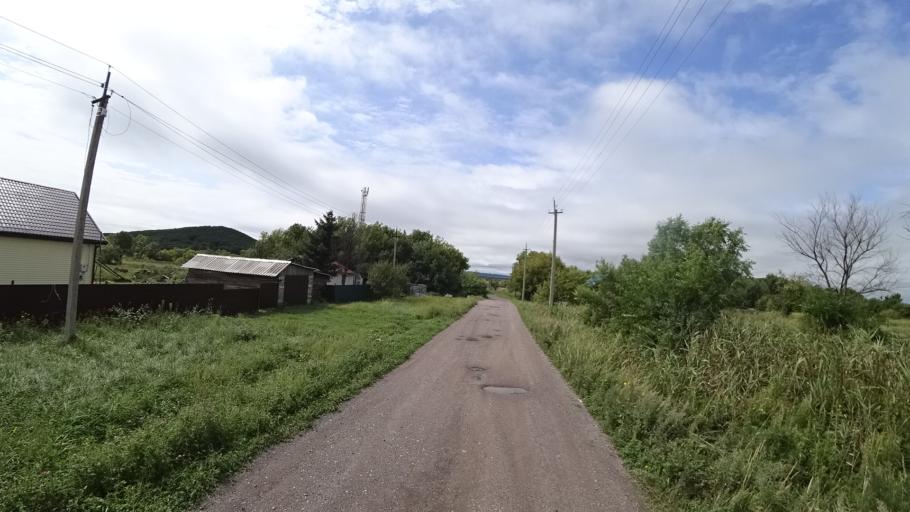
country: RU
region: Primorskiy
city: Lyalichi
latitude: 44.1401
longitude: 132.3769
